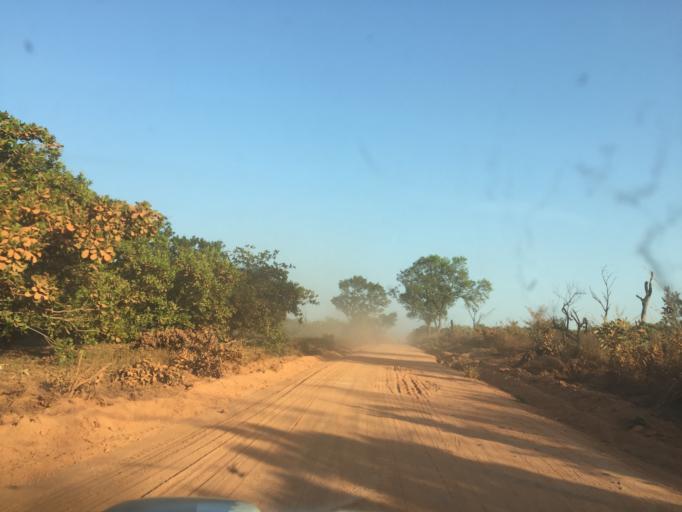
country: GW
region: Oio
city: Farim
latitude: 12.5313
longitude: -15.2743
